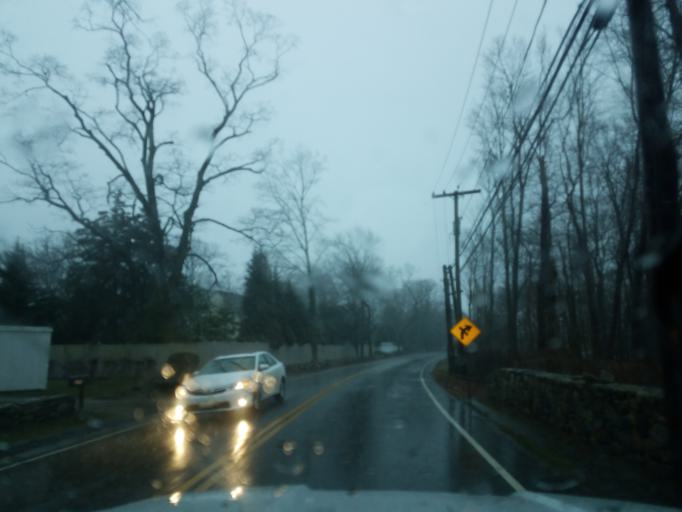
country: US
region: Connecticut
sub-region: Fairfield County
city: Darien
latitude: 41.0895
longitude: -73.4738
